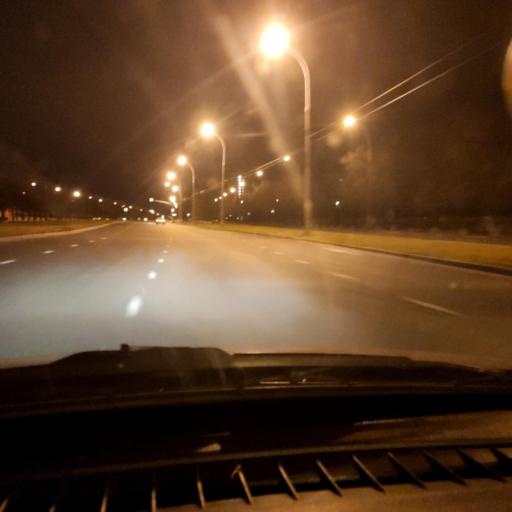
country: RU
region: Samara
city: Tol'yatti
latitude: 53.5193
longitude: 49.2819
